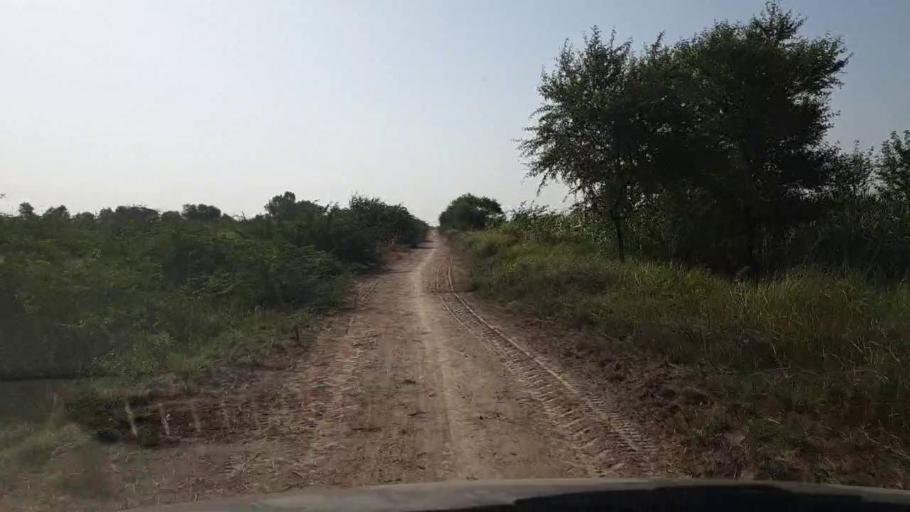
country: PK
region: Sindh
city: Kadhan
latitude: 24.5997
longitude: 69.0749
